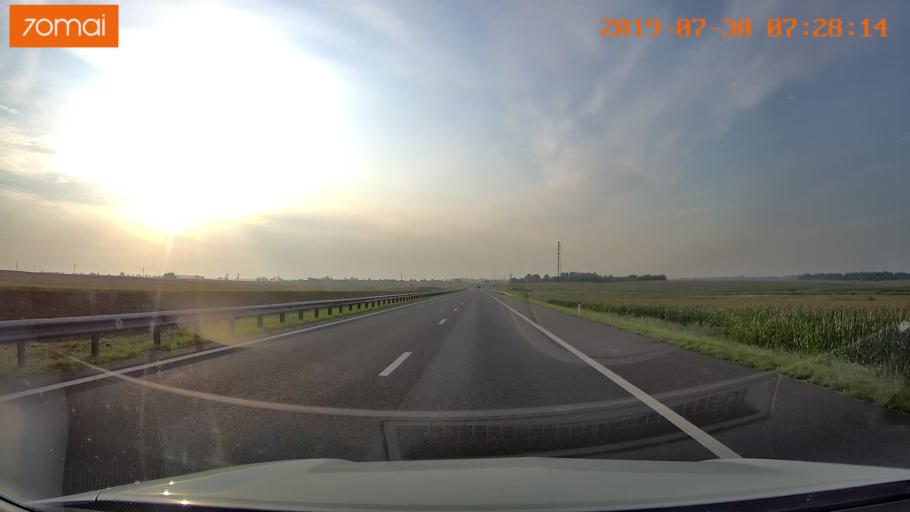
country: RU
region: Kaliningrad
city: Gvardeysk
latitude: 54.6783
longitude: 20.9077
